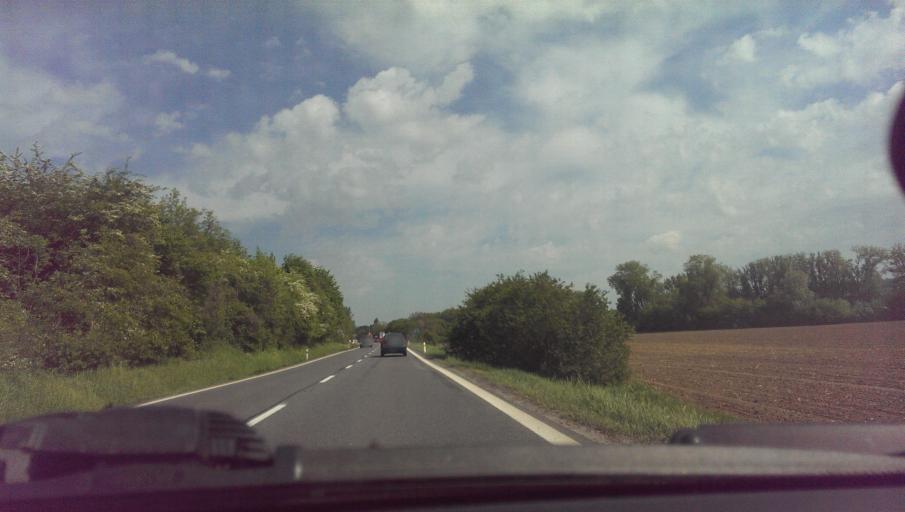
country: CZ
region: Zlin
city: Spytihnev
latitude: 49.1566
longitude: 17.5044
